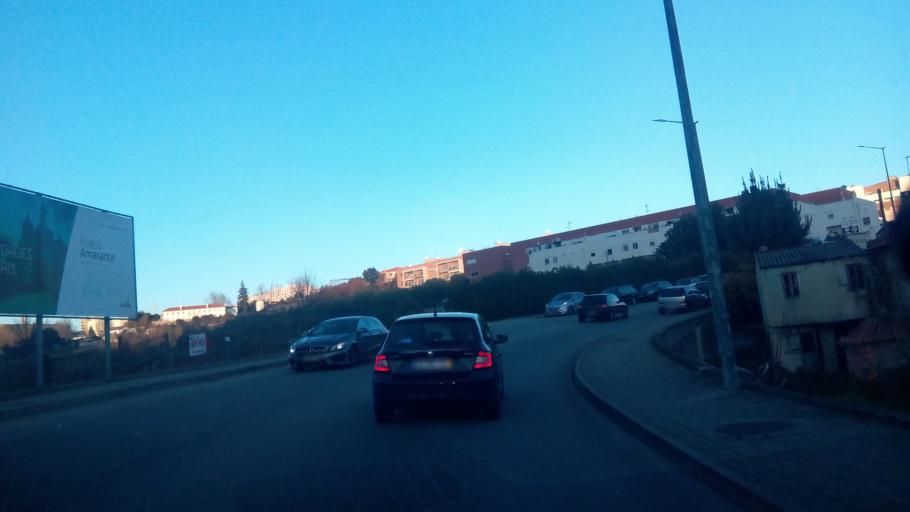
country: PT
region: Porto
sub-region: Amarante
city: Amarante
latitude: 41.2737
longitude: -8.0888
